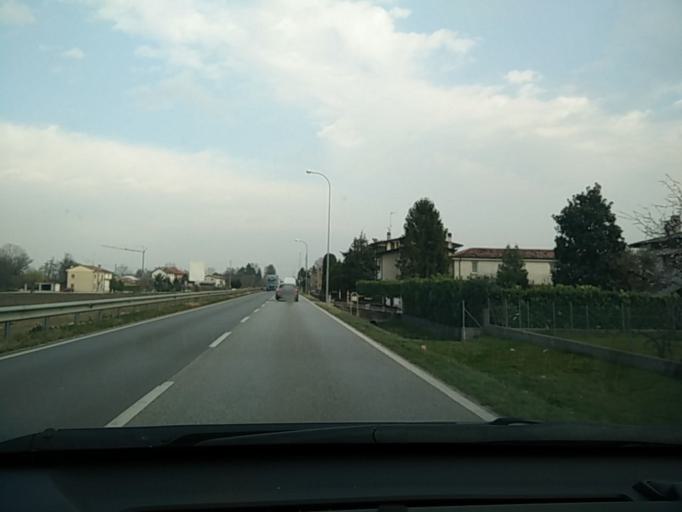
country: IT
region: Veneto
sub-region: Provincia di Treviso
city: Cosniga-Zoppe
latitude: 45.8696
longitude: 12.3798
